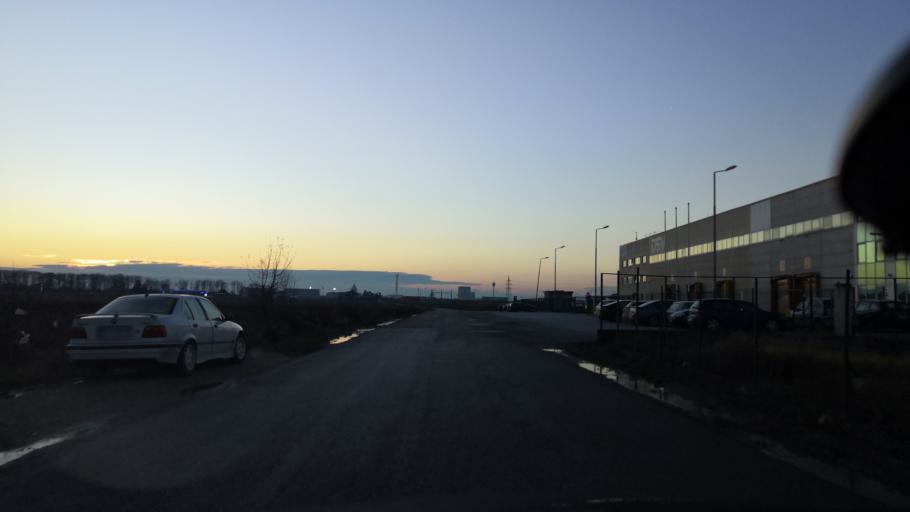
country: RS
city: Simanovci
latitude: 44.8818
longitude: 20.1295
